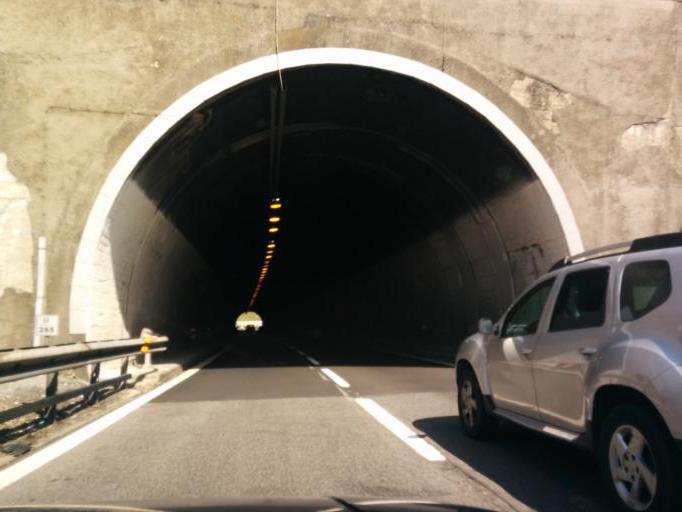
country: IT
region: Tuscany
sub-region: Province of Florence
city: Cavallina
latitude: 43.9522
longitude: 11.2129
